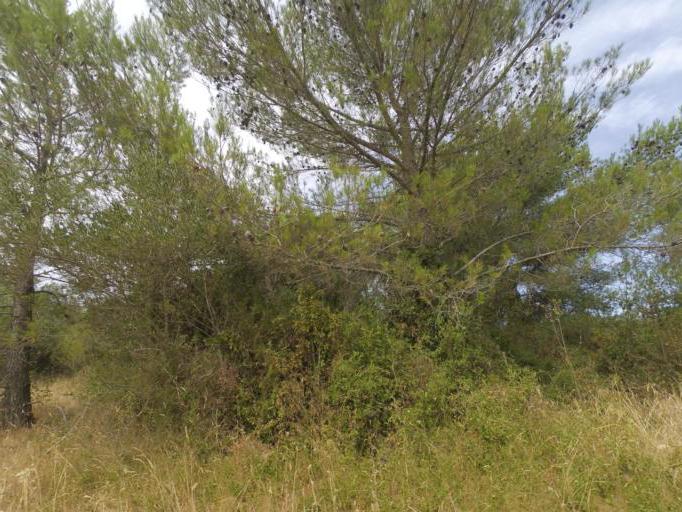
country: FR
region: Languedoc-Roussillon
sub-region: Departement du Gard
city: Congenies
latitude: 43.7614
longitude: 4.1608
